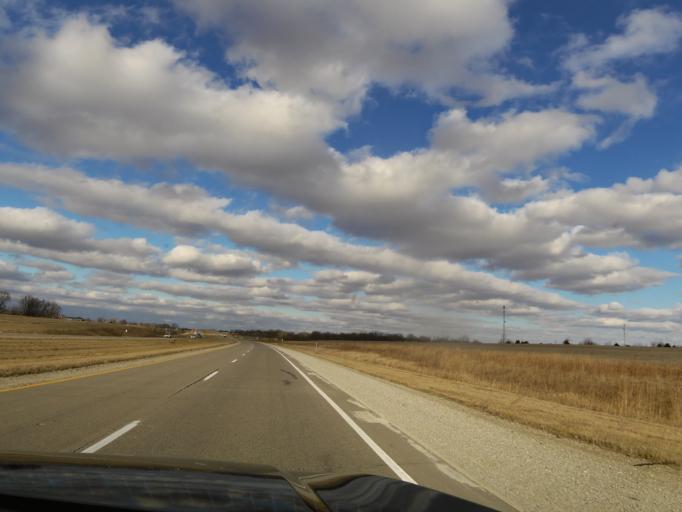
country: US
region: Illinois
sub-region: Hancock County
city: Nauvoo
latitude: 40.5192
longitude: -91.5635
